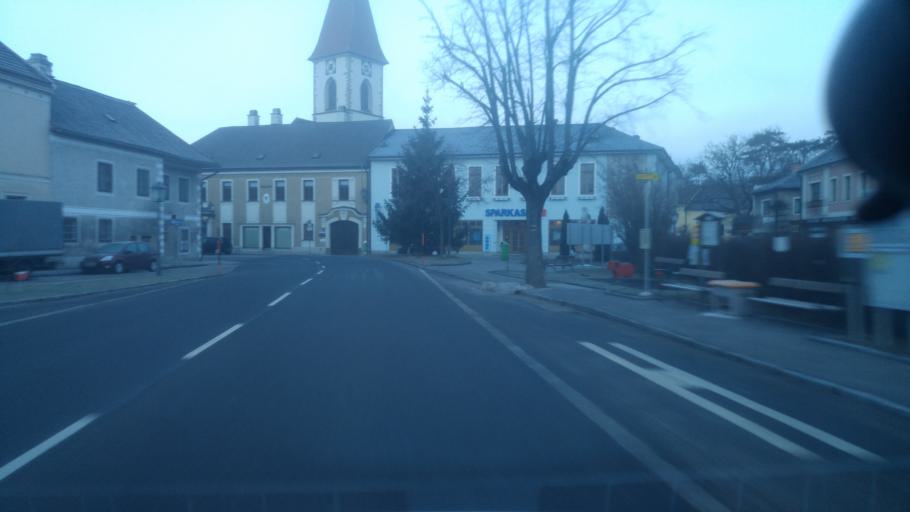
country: AT
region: Lower Austria
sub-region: Politischer Bezirk Baden
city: Pottenstein
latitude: 47.9584
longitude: 16.0972
